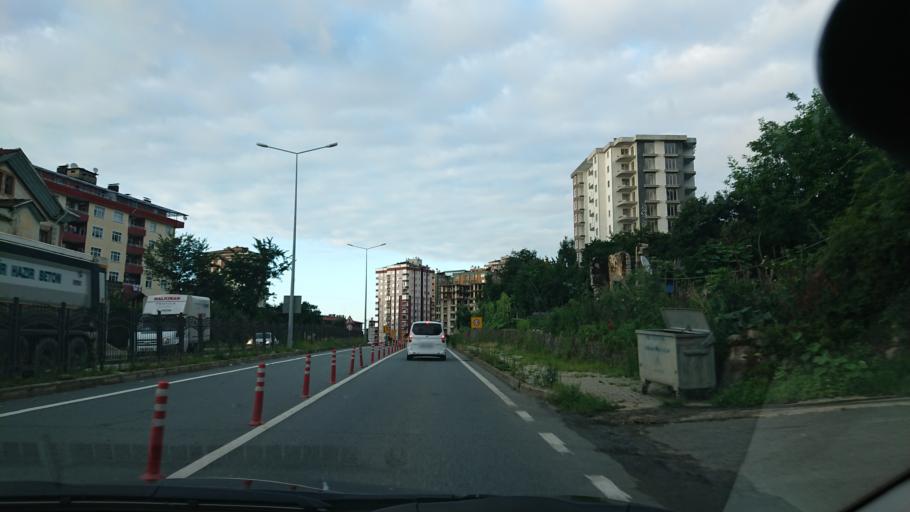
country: TR
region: Rize
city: Gundogdu
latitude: 41.0351
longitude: 40.5646
